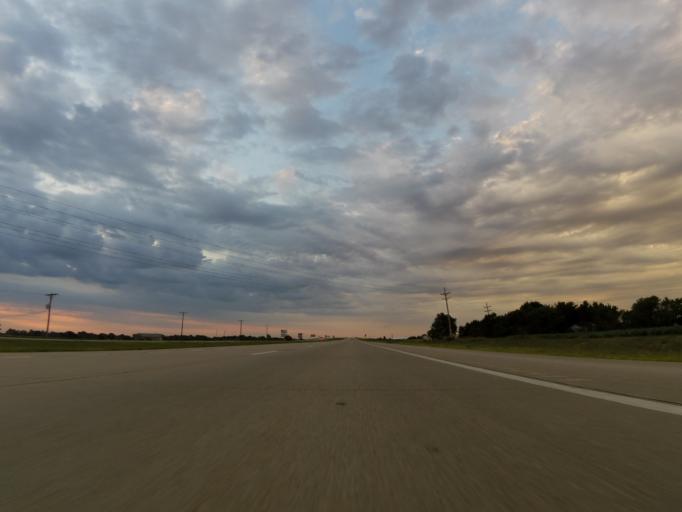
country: US
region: Kansas
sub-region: Reno County
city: South Hutchinson
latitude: 37.9457
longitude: -97.8858
